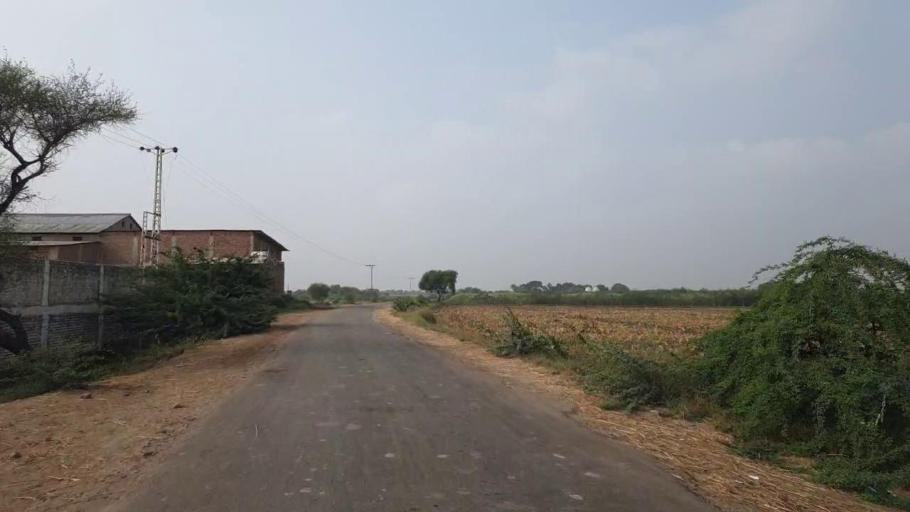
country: PK
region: Sindh
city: Matli
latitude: 24.9983
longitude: 68.6525
